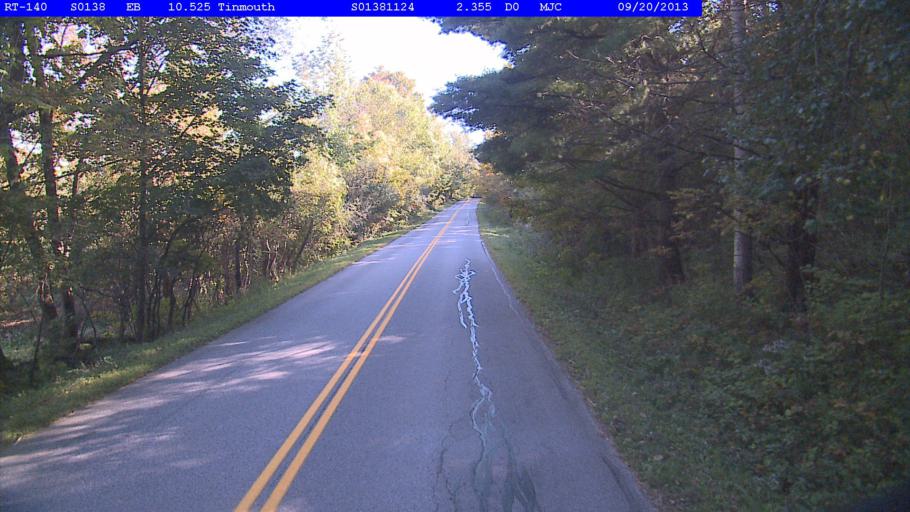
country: US
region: Vermont
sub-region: Rutland County
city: West Rutland
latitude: 43.4614
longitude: -73.0474
